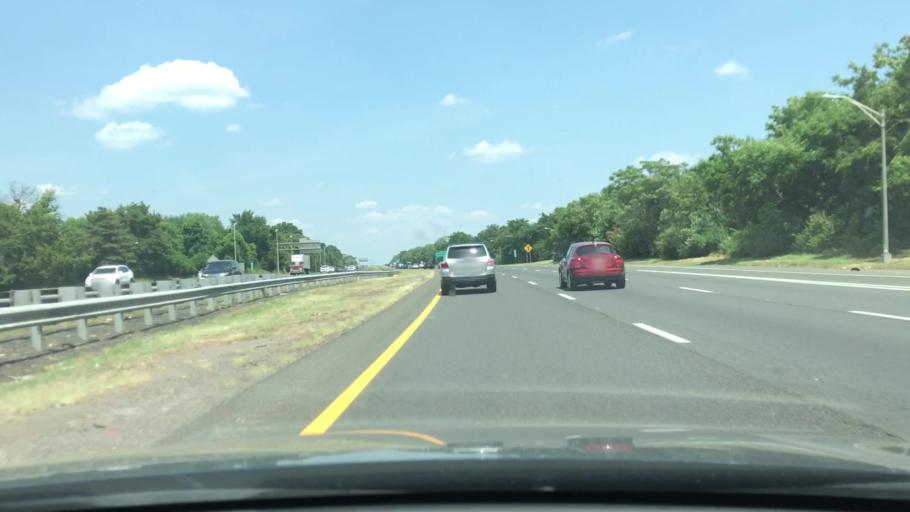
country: US
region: New Jersey
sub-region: Somerset County
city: South Bound Brook
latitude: 40.5413
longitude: -74.5066
